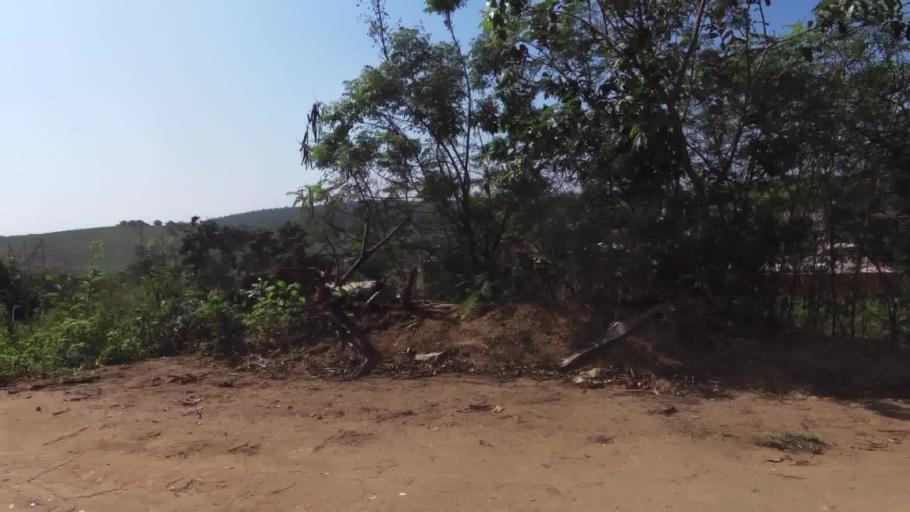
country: BR
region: Espirito Santo
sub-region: Marataizes
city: Marataizes
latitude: -21.0302
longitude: -40.8249
